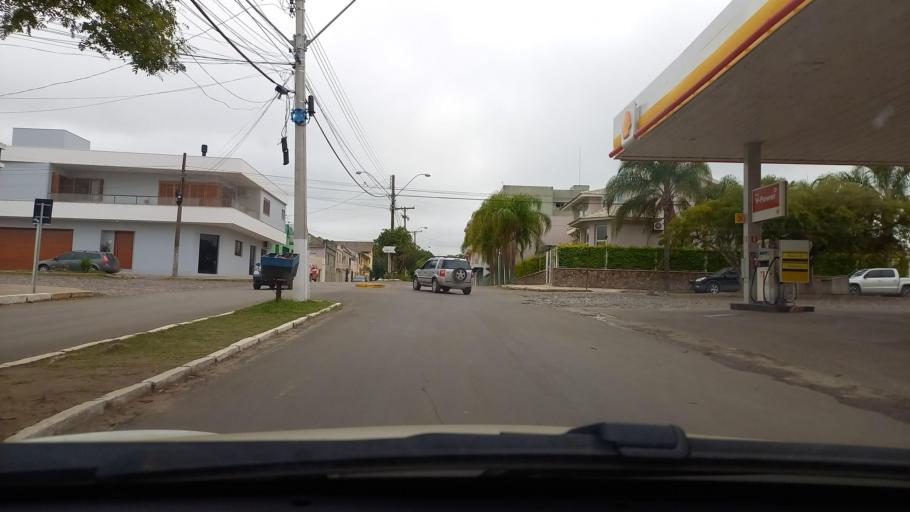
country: BR
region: Rio Grande do Sul
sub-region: Dom Pedrito
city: Dom Pedrito
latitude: -30.9759
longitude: -54.6732
